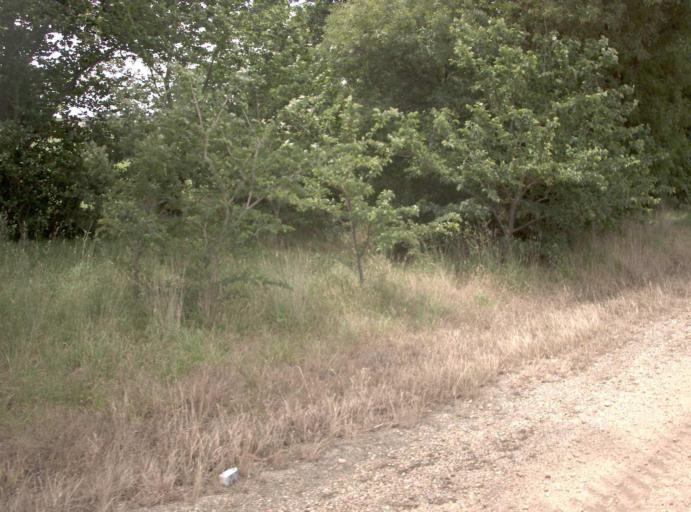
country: AU
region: Victoria
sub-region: Wellington
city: Sale
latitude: -37.9886
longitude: 146.9954
